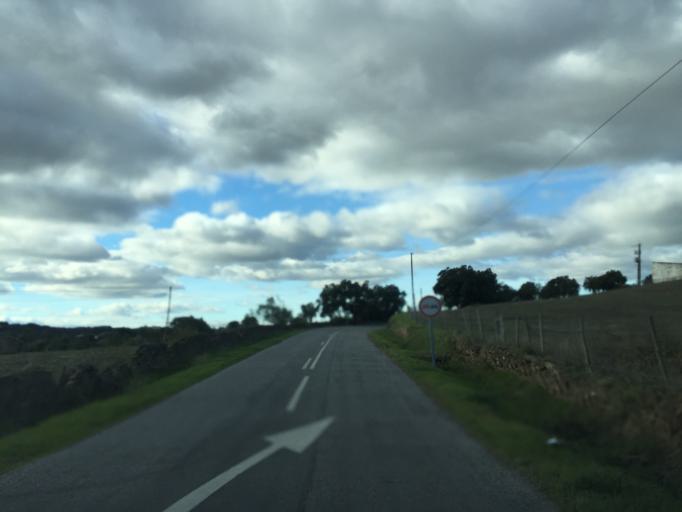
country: PT
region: Portalegre
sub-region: Alter do Chao
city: Alter do Chao
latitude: 39.2738
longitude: -7.6384
